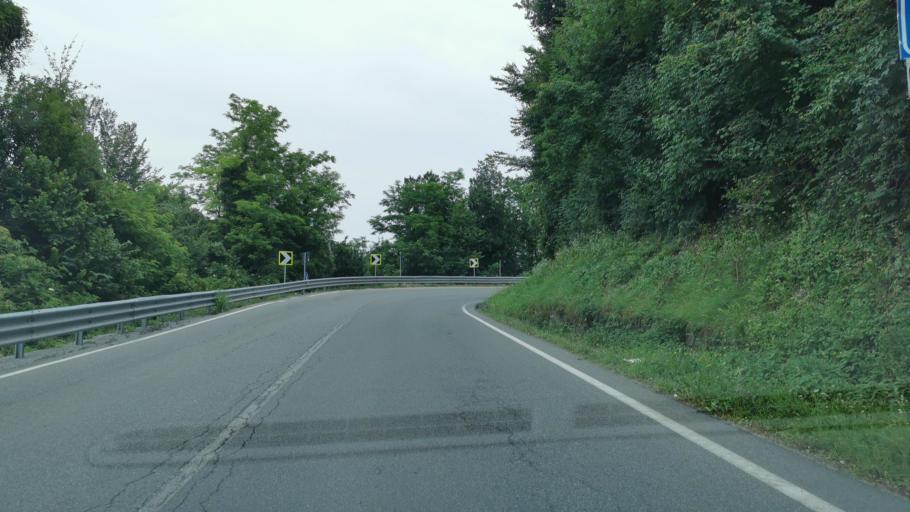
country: IT
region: Piedmont
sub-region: Provincia di Cuneo
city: Ceva
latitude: 44.3803
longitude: 8.0407
